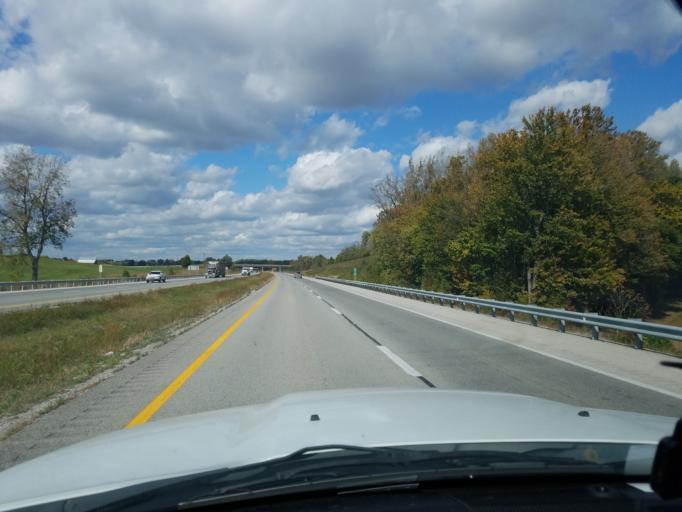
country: US
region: Kentucky
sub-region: Daviess County
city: Masonville
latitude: 37.7135
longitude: -87.0483
